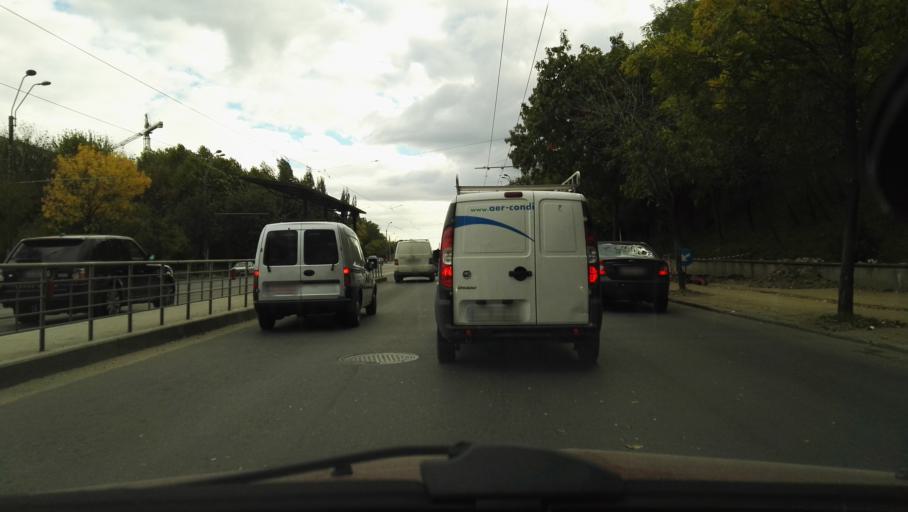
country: RO
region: Bucuresti
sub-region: Municipiul Bucuresti
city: Bucharest
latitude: 44.3978
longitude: 26.1208
